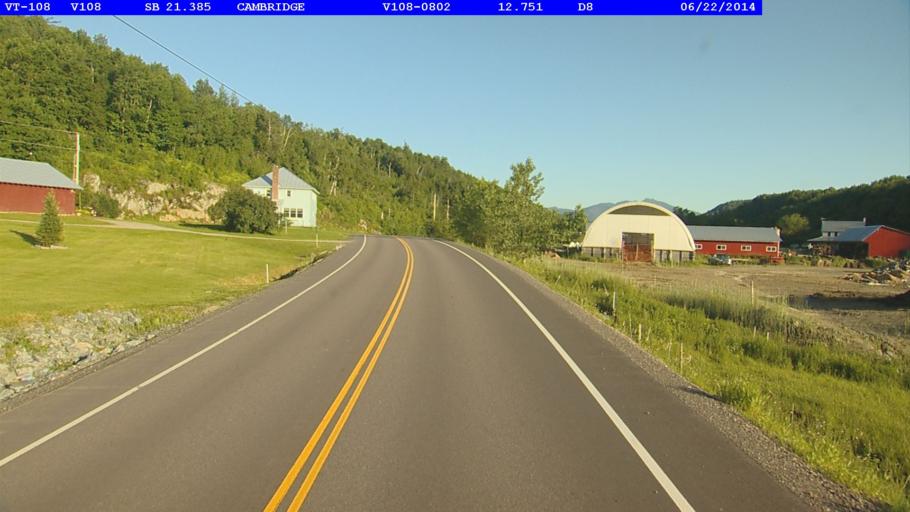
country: US
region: Vermont
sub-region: Lamoille County
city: Johnson
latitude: 44.6986
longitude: -72.8291
